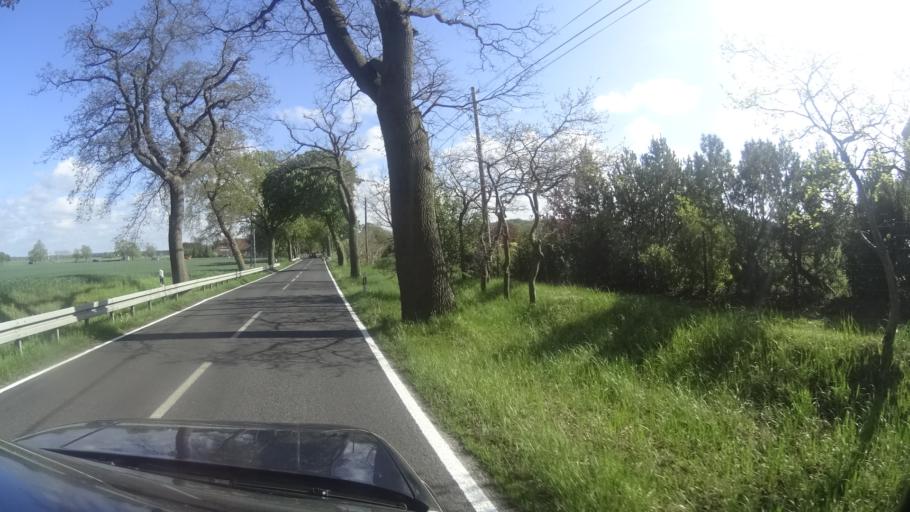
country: DE
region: Mecklenburg-Vorpommern
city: Gelbensande
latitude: 54.2396
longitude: 12.3200
